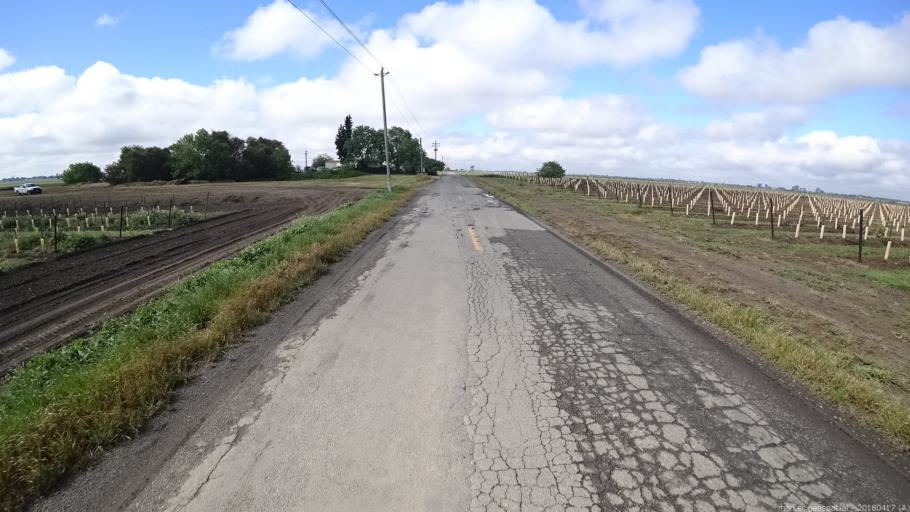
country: US
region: California
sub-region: Sacramento County
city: Walnut Grove
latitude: 38.2670
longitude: -121.5473
